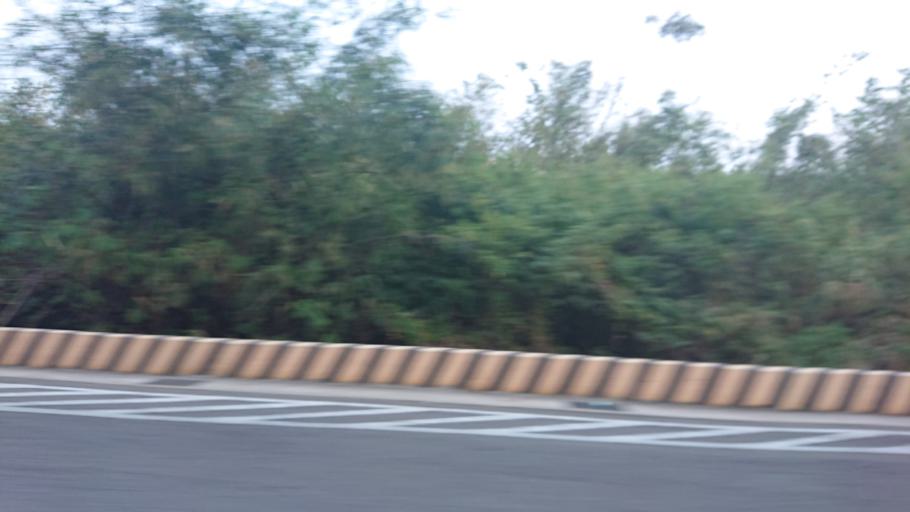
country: TW
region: Fukien
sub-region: Kinmen
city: Jincheng
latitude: 24.4483
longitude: 118.3308
